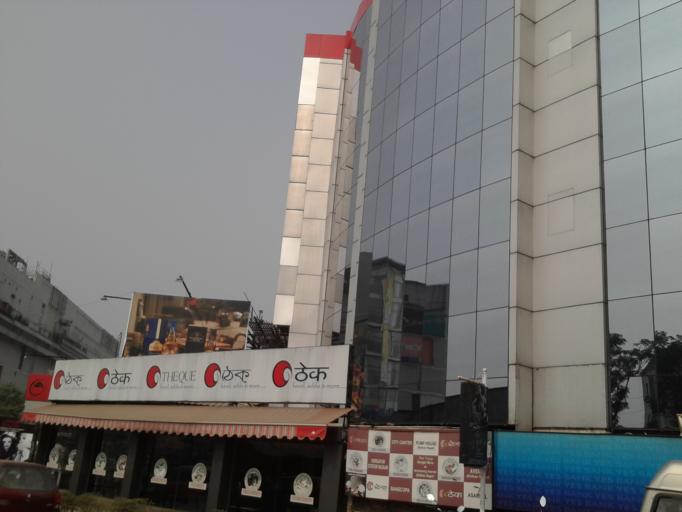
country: IN
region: West Bengal
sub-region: Barddhaman
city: Durgapur
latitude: 23.5390
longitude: 87.2927
